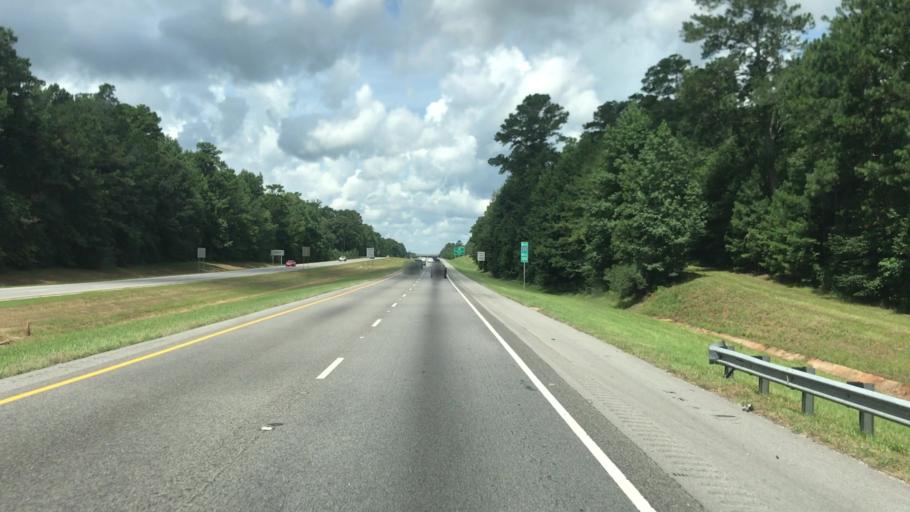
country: US
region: Georgia
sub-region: Walton County
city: Social Circle
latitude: 33.6057
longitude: -83.6768
